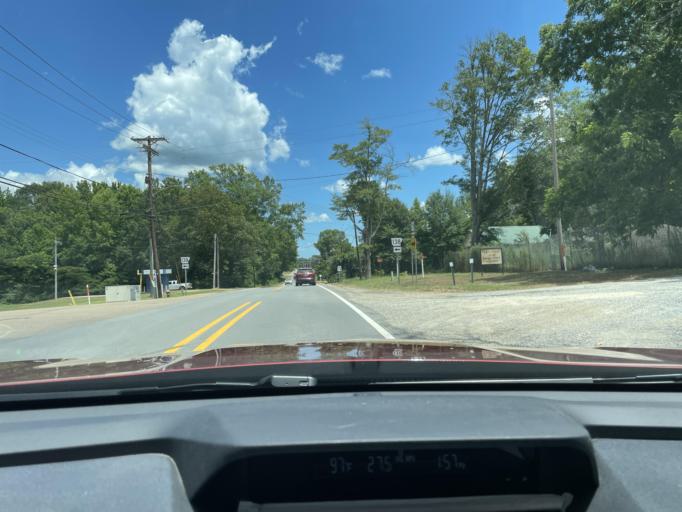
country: US
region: Arkansas
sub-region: Drew County
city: Monticello
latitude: 33.6286
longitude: -91.7747
